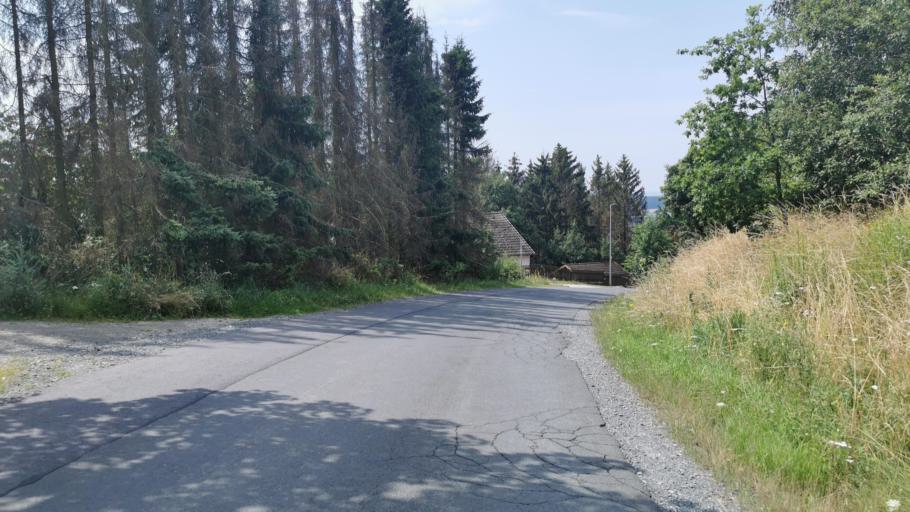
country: DE
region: Bavaria
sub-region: Upper Franconia
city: Marktrodach
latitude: 50.2792
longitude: 11.3837
